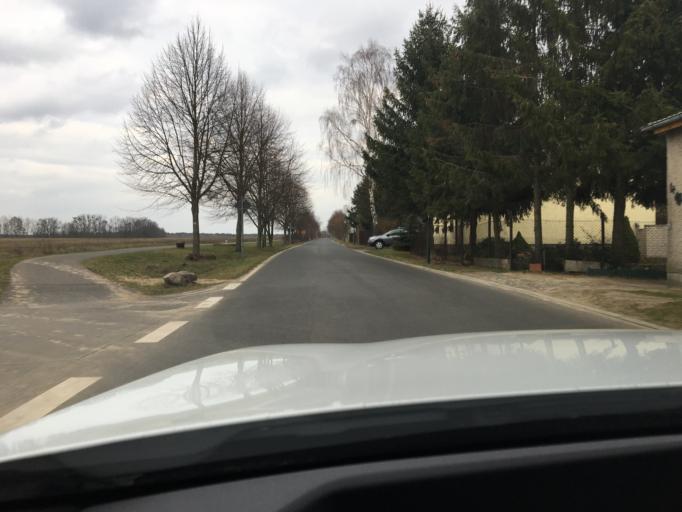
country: DE
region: Brandenburg
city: Liebenwalde
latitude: 52.8811
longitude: 13.4474
